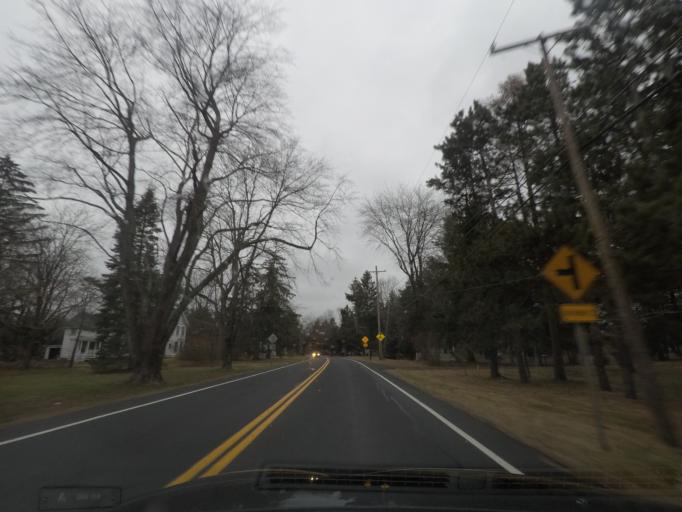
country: US
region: New York
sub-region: Rensselaer County
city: East Greenbush
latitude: 42.6030
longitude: -73.6499
